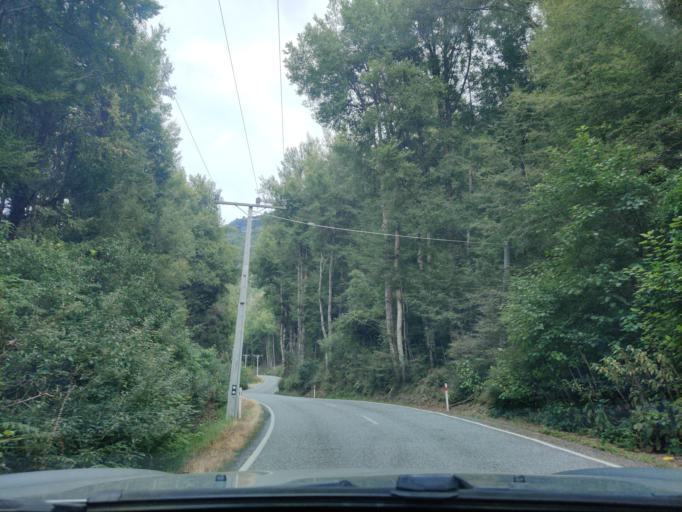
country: NZ
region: Otago
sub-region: Queenstown-Lakes District
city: Queenstown
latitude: -45.0702
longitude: 168.5032
